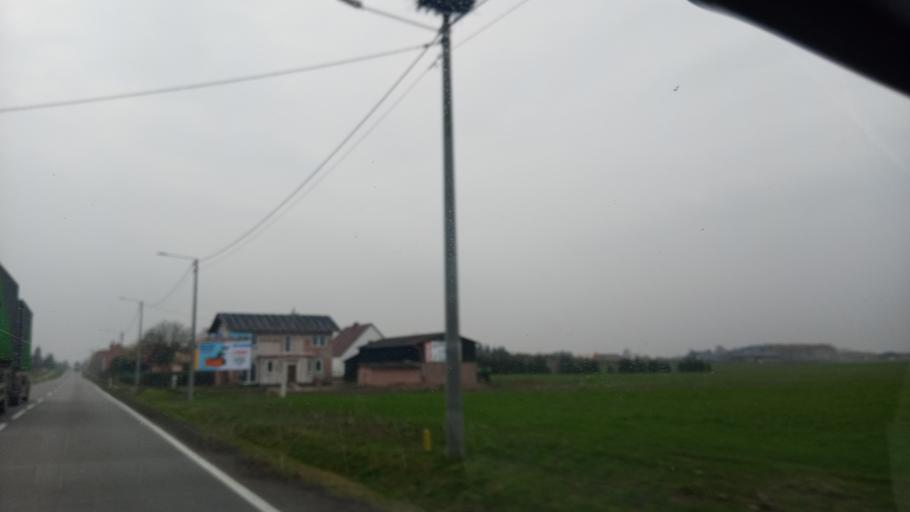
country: PL
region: Pomeranian Voivodeship
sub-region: Powiat czluchowski
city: Czluchow
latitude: 53.6822
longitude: 17.3351
